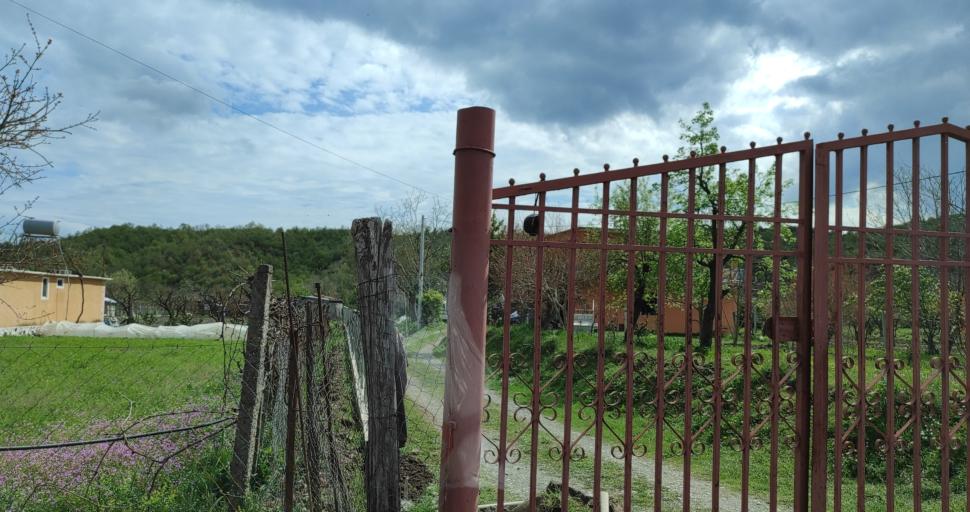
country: AL
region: Shkoder
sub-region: Rrethi i Shkodres
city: Dajc
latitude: 42.0339
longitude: 19.4101
